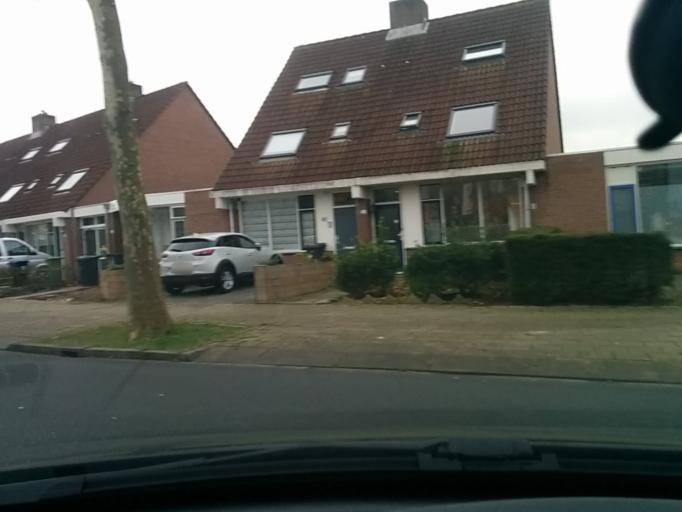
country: NL
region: Gelderland
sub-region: Gemeente Arnhem
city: Sterrenberg
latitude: 51.9493
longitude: 5.8757
